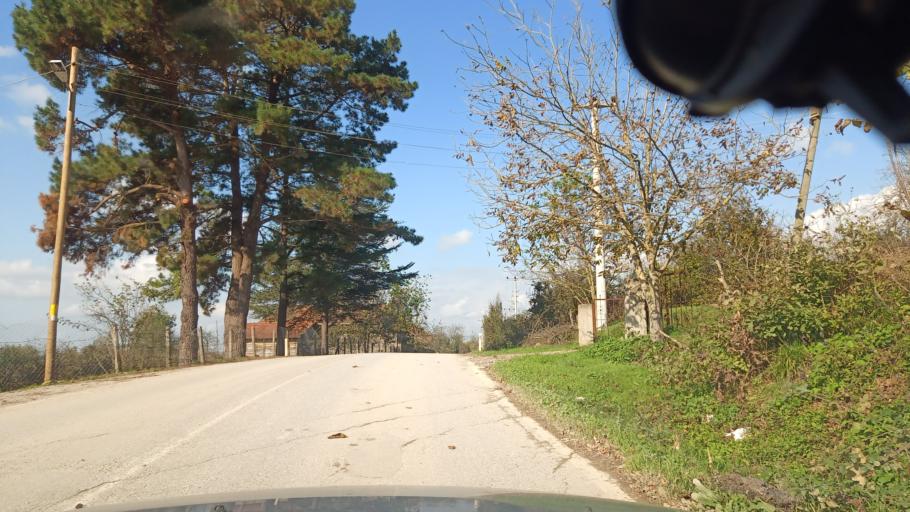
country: TR
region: Sakarya
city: Kaynarca
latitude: 41.0952
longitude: 30.4396
